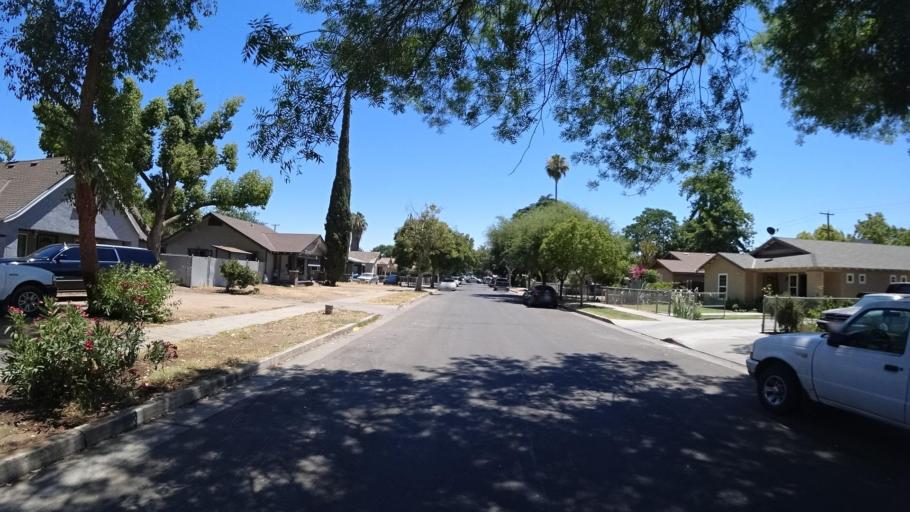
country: US
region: California
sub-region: Fresno County
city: Fresno
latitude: 36.7386
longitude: -119.7491
